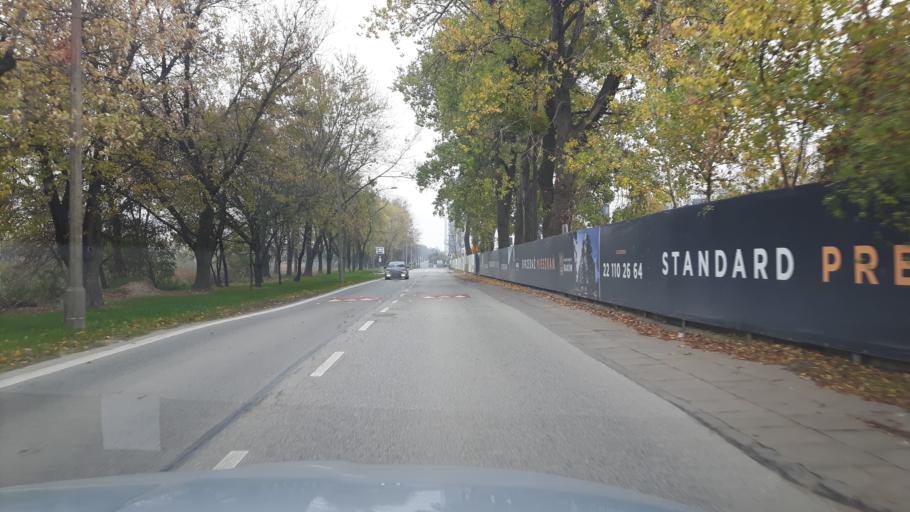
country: PL
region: Masovian Voivodeship
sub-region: Warszawa
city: Wlochy
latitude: 52.1987
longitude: 20.9564
